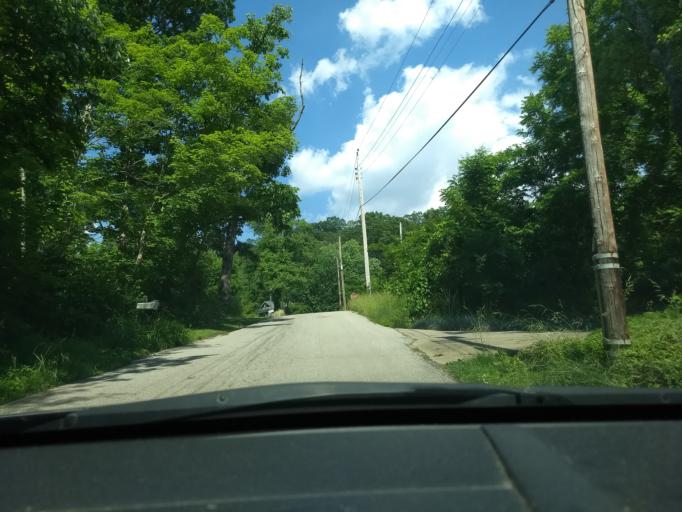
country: US
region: Indiana
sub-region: Floyd County
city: New Albany
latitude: 38.2626
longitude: -85.8620
